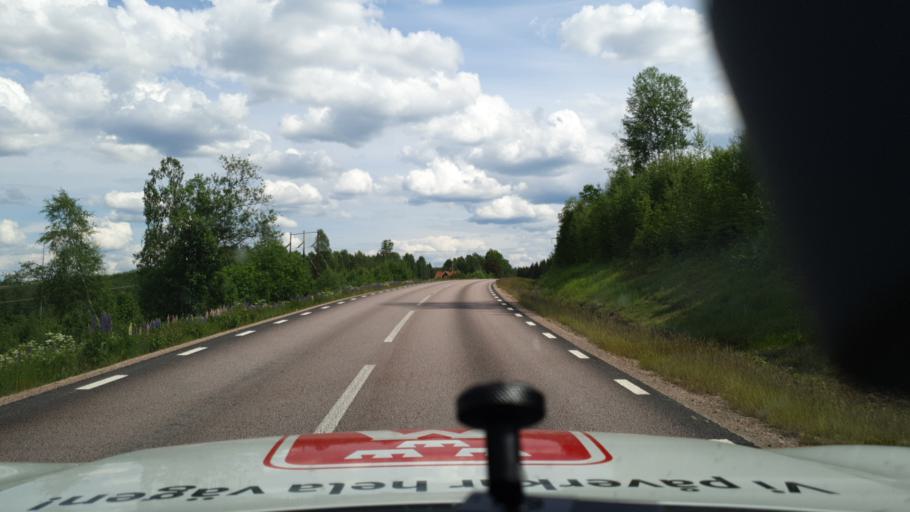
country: SE
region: Vaermland
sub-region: Torsby Kommun
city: Torsby
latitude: 60.1305
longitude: 12.9757
